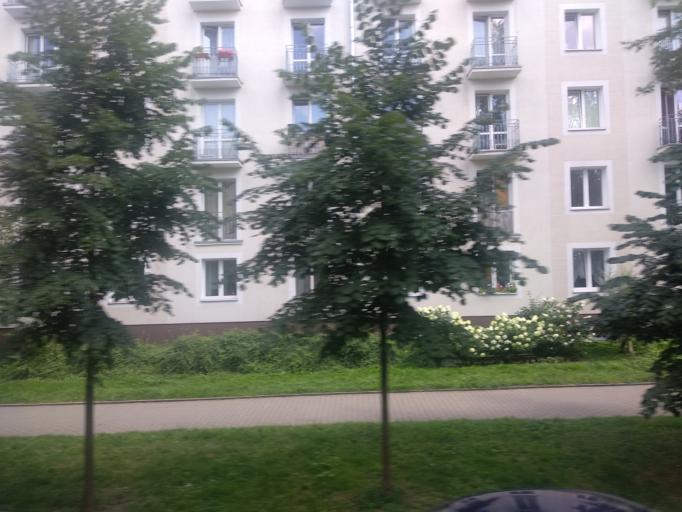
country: PL
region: Masovian Voivodeship
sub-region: Warszawa
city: Wola
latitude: 52.2521
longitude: 20.9950
